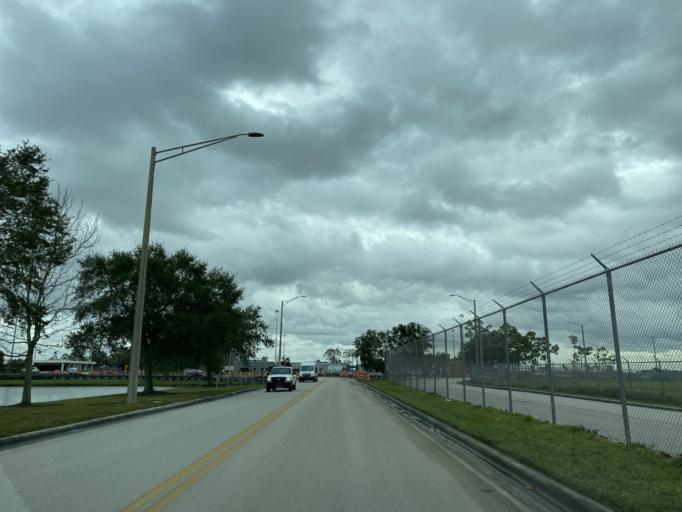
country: US
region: Florida
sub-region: Orange County
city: Belle Isle
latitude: 28.4407
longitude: -81.3046
